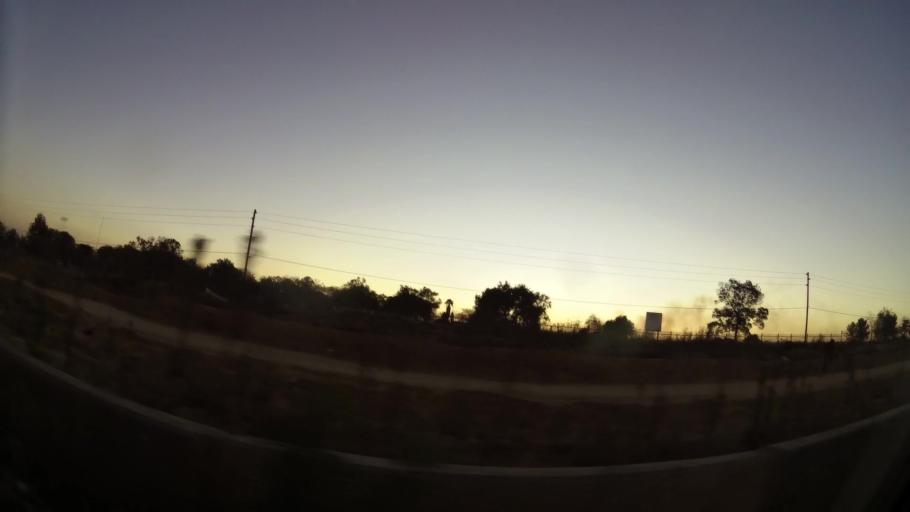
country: ZA
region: Gauteng
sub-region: City of Johannesburg Metropolitan Municipality
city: Diepsloot
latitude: -25.9450
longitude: 28.0196
